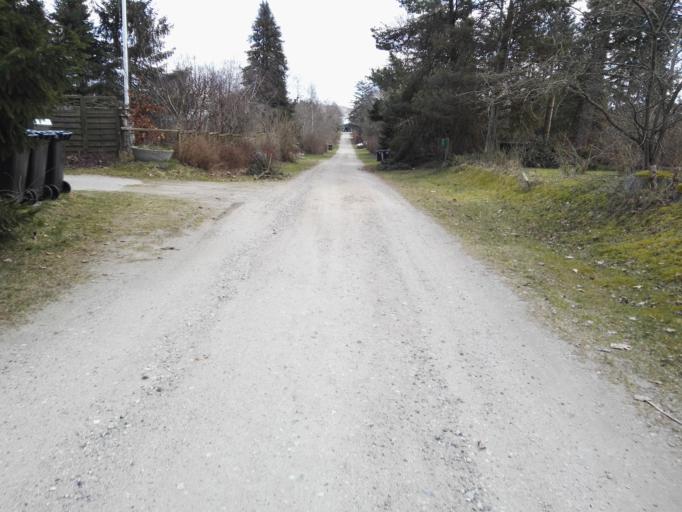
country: DK
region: Zealand
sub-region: Lejre Kommune
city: Ejby
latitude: 55.7627
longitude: 11.8277
